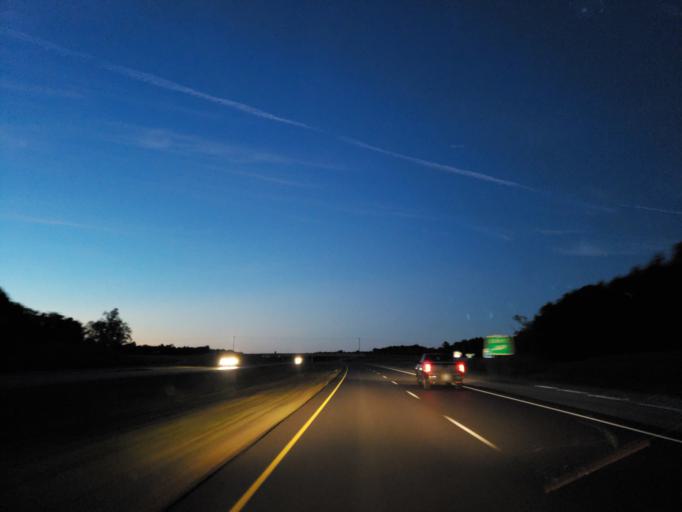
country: US
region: Mississippi
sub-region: Clarke County
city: Quitman
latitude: 32.0550
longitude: -88.6770
